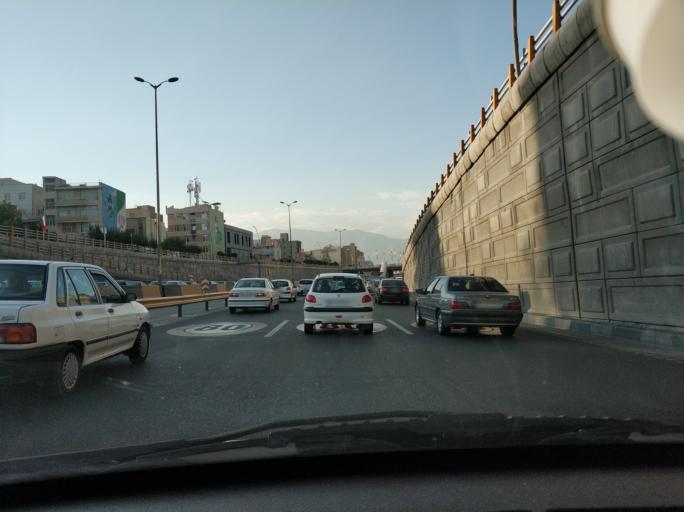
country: IR
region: Tehran
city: Tehran
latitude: 35.6946
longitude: 51.4568
